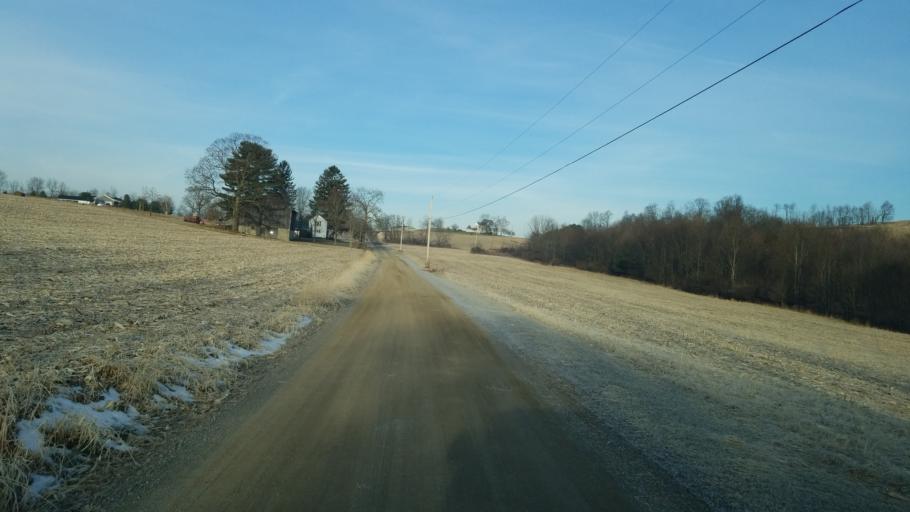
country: US
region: Pennsylvania
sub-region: Indiana County
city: Chevy Chase Heights
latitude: 40.8454
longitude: -79.2574
